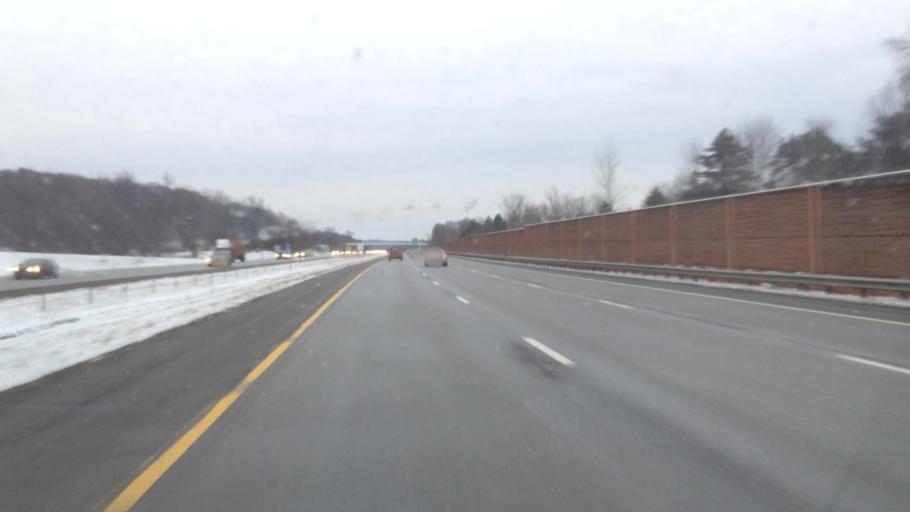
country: US
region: Ohio
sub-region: Medina County
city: Brunswick
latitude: 41.2218
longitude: -81.7939
